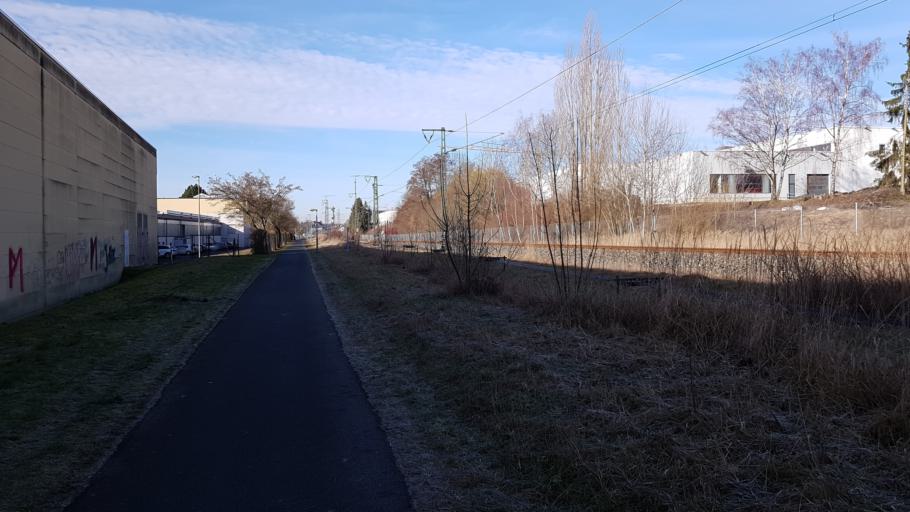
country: DE
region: Bavaria
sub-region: Upper Franconia
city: Rodental
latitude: 50.2899
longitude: 11.0409
